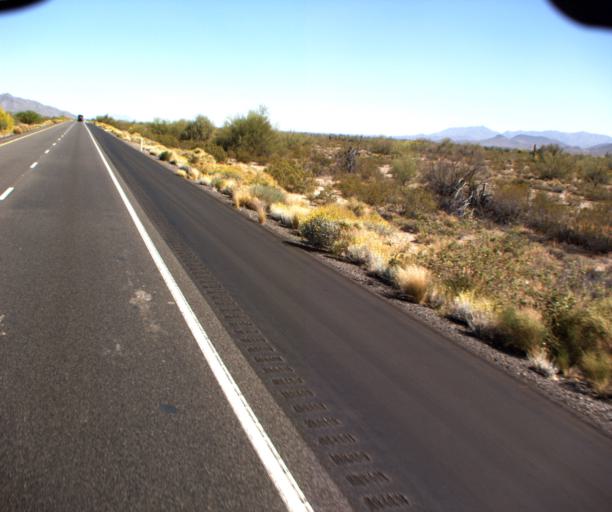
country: US
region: Arizona
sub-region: Maricopa County
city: Gila Bend
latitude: 32.8905
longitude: -112.4843
